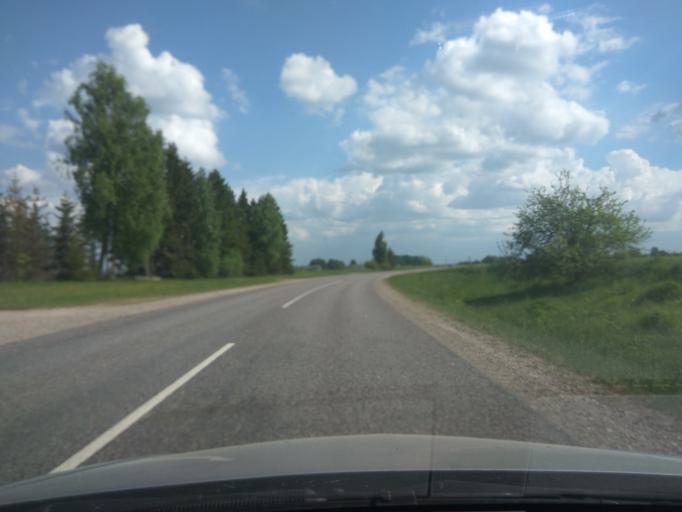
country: LV
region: Kuldigas Rajons
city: Kuldiga
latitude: 57.0179
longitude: 21.8745
